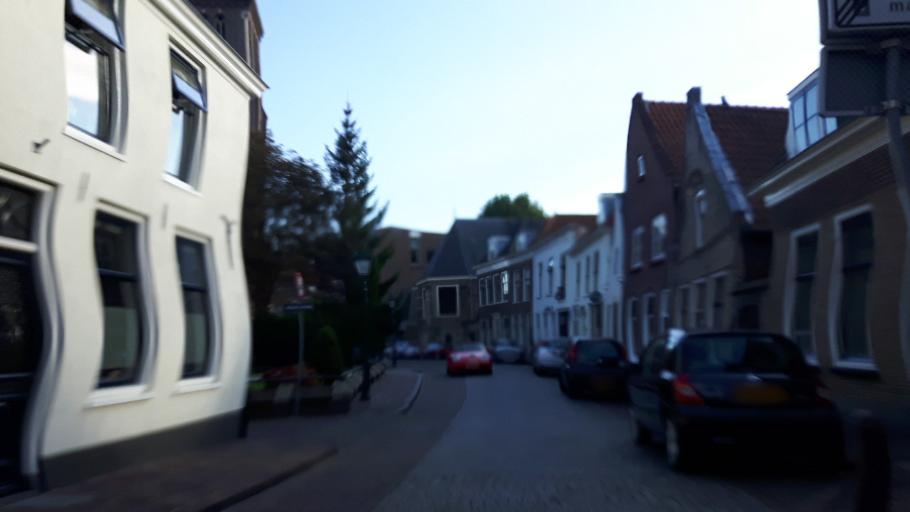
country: NL
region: Utrecht
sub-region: Gemeente Oudewater
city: Oudewater
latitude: 52.0221
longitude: 4.8727
